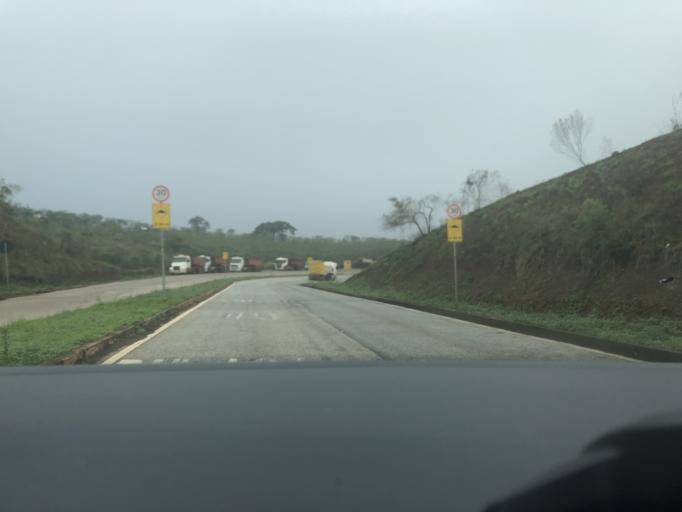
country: BR
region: Minas Gerais
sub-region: Congonhas
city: Congonhas
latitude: -20.5949
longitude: -43.9567
